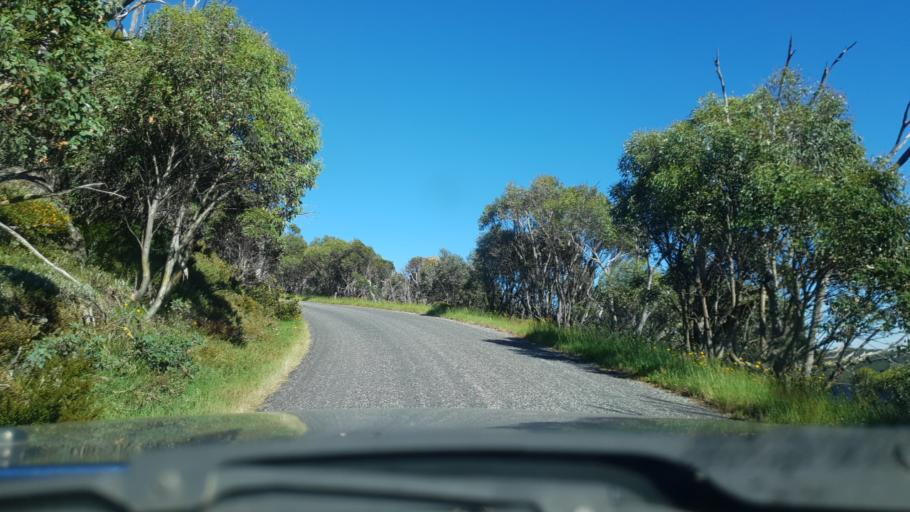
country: AU
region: Victoria
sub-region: Alpine
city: Mount Beauty
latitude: -36.8911
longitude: 147.3057
